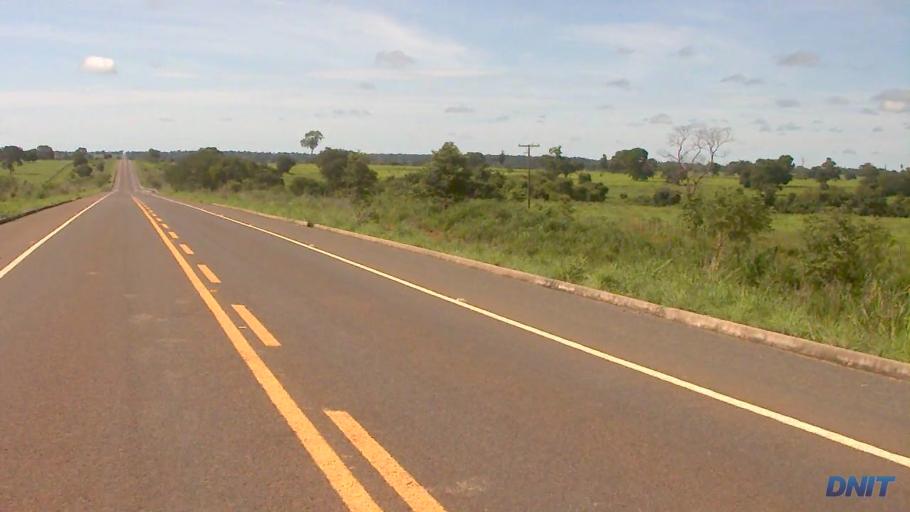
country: BR
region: Goias
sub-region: Sao Miguel Do Araguaia
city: Sao Miguel do Araguaia
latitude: -13.3587
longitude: -50.1472
